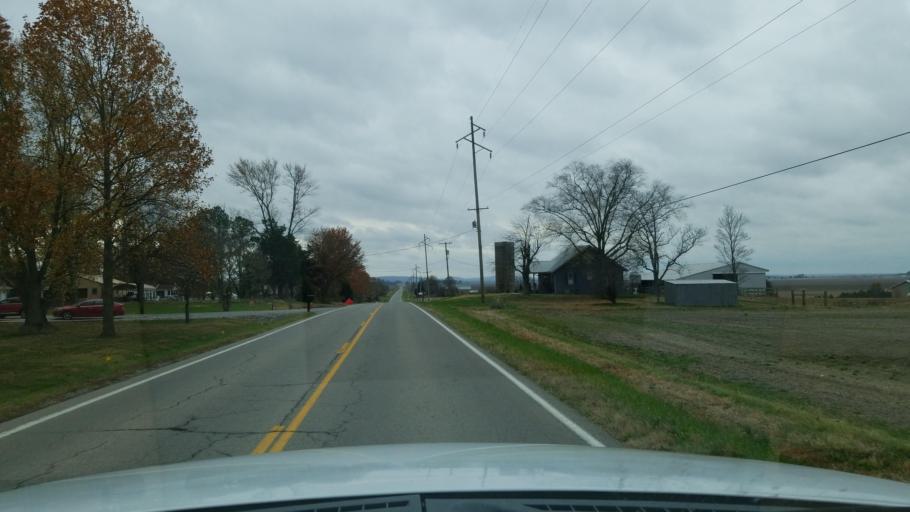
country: US
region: Illinois
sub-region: Saline County
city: Eldorado
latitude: 37.7930
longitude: -88.4382
